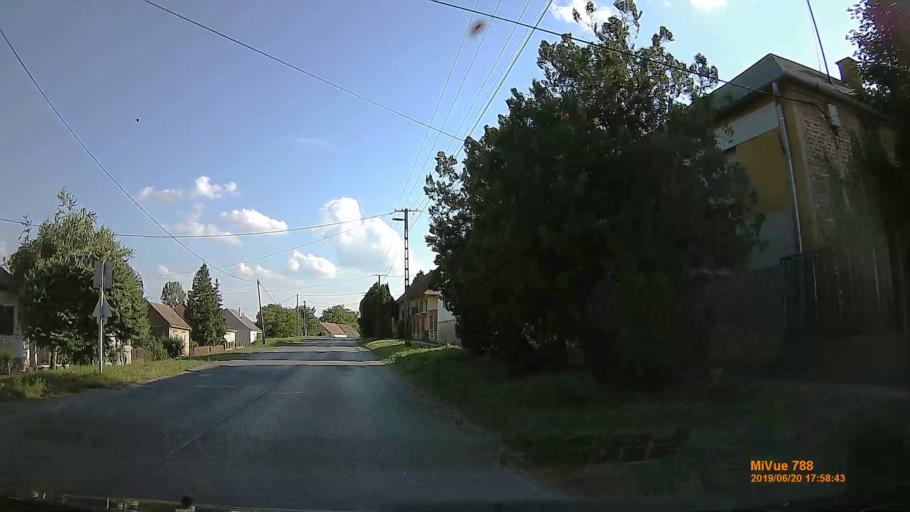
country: HU
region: Baranya
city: Buekkoesd
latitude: 46.1026
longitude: 17.9894
